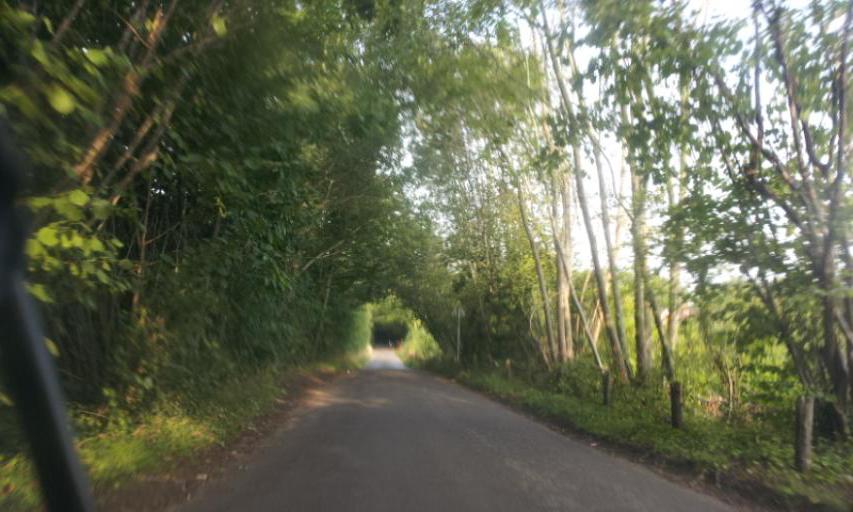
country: GB
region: England
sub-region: Kent
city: Wateringbury
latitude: 51.2664
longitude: 0.4379
